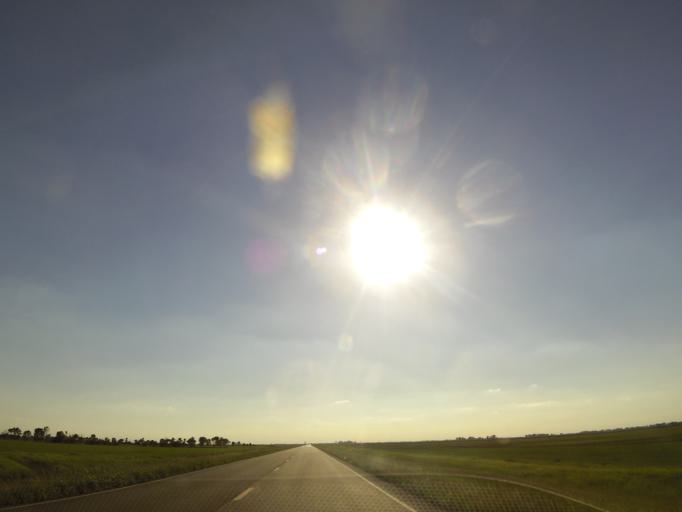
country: US
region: North Dakota
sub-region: Grand Forks County
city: Grand Forks Air Force Base
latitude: 48.1357
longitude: -97.2238
